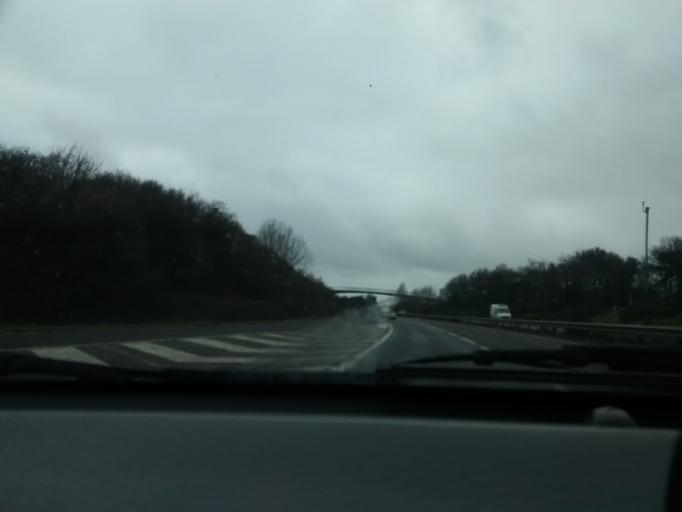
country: GB
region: England
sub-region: Suffolk
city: Felixstowe
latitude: 51.9929
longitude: 1.3159
